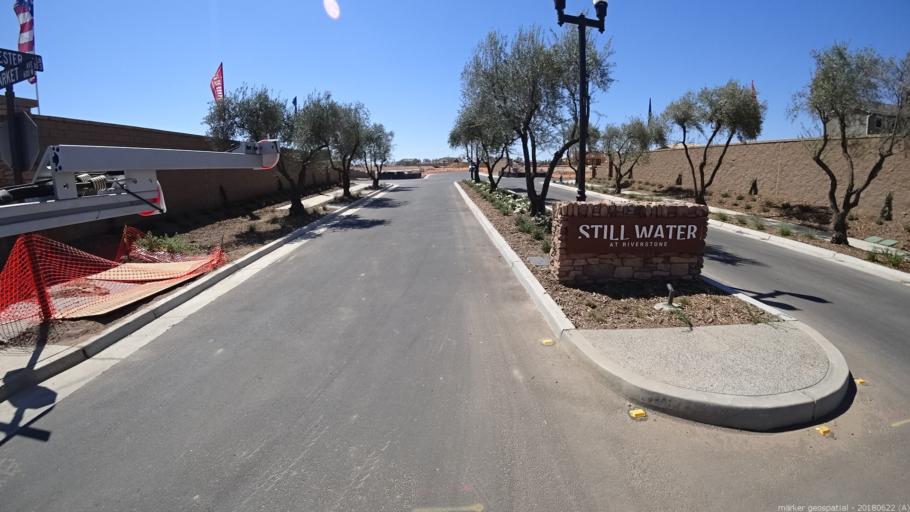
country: US
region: California
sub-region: Madera County
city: Bonadelle Ranchos-Madera Ranchos
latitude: 36.9183
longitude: -119.8034
